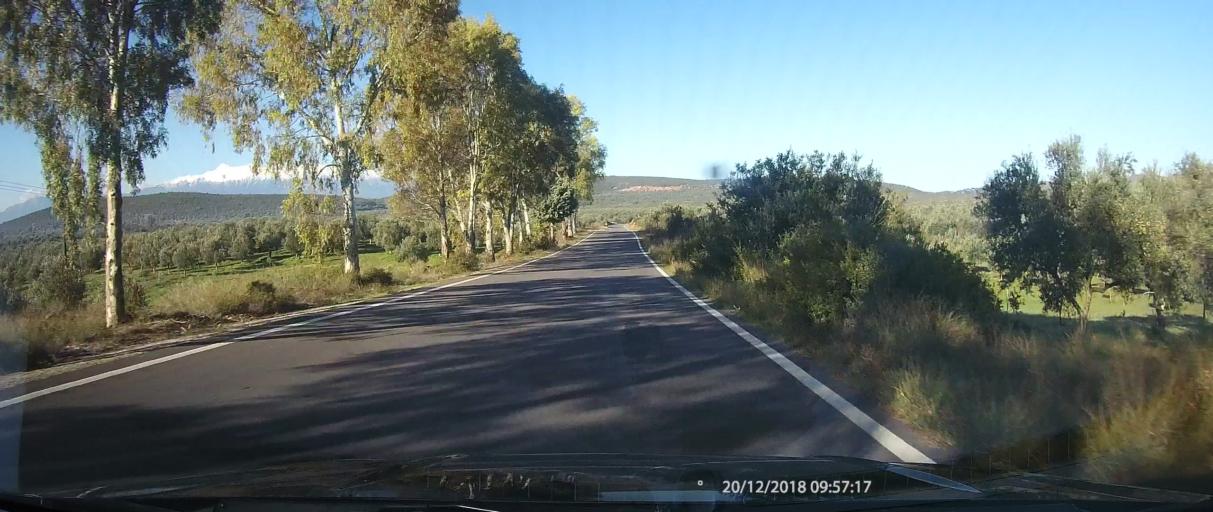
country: GR
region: Peloponnese
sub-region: Nomos Lakonias
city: Yerakion
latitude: 37.0219
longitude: 22.5990
